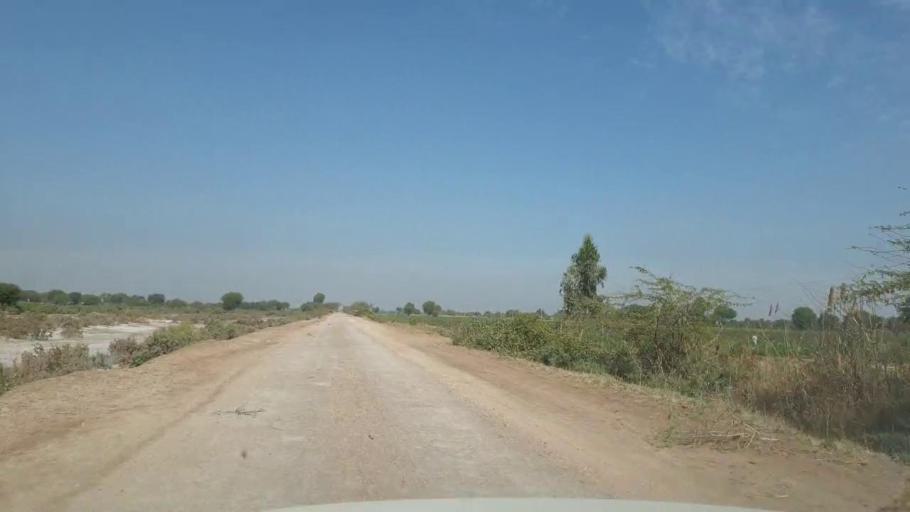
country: PK
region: Sindh
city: Pithoro
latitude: 25.5806
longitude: 69.2010
